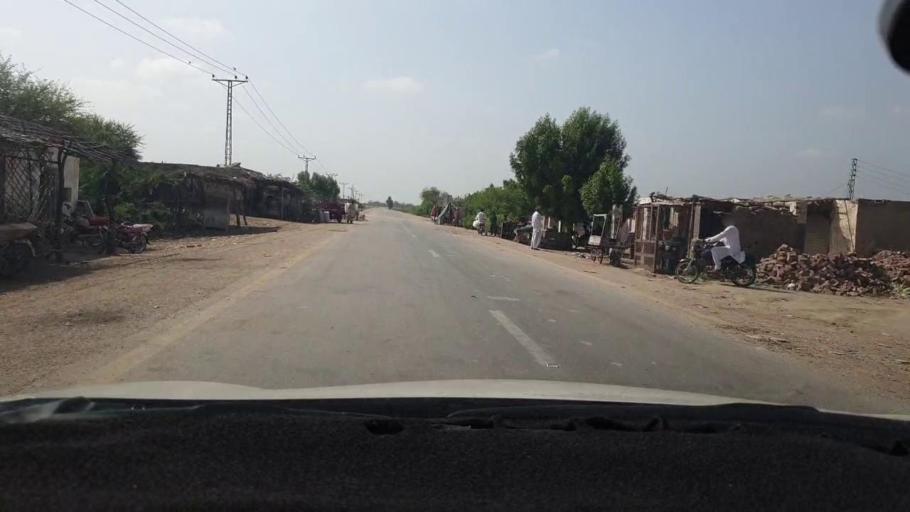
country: PK
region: Sindh
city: Mirpur Khas
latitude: 25.7544
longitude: 69.0847
